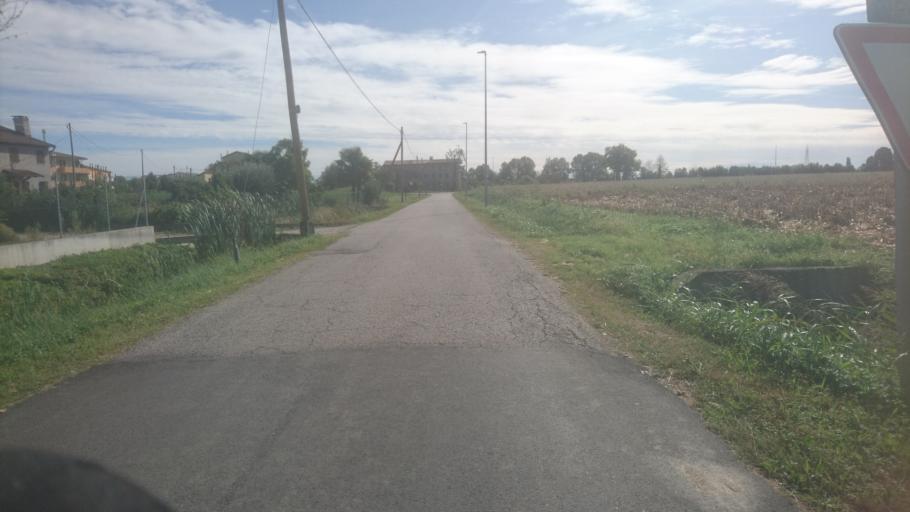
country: IT
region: Veneto
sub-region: Provincia di Padova
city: Veggiano
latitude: 45.4452
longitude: 11.7055
